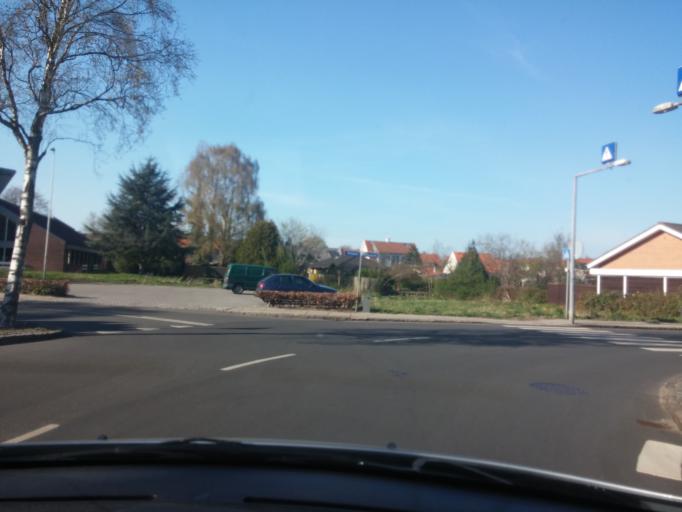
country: DK
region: Central Jutland
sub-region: Odder Kommune
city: Odder
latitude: 55.9730
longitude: 10.1534
